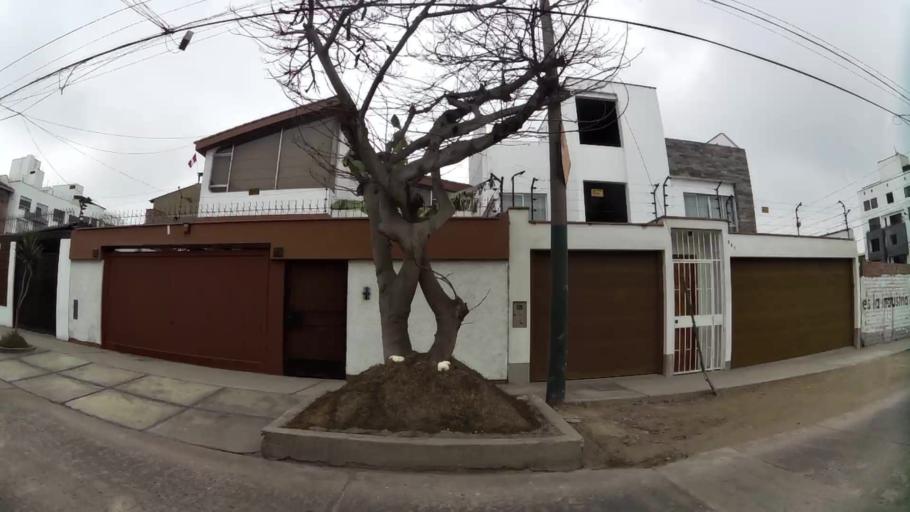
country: PE
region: Lima
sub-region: Lima
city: Surco
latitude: -12.1214
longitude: -76.9869
